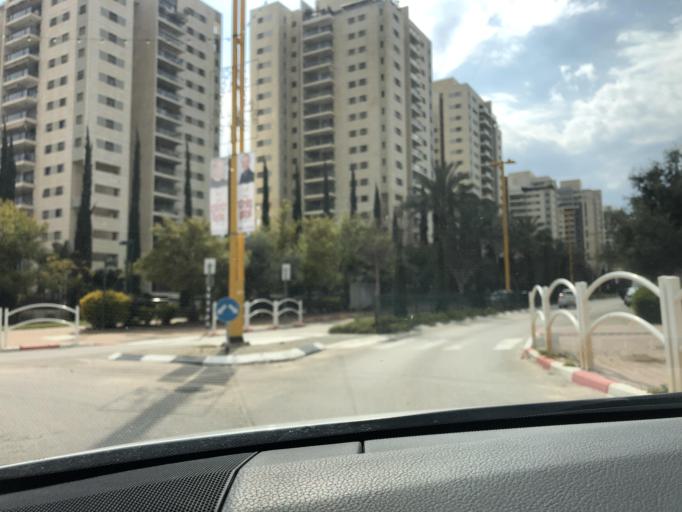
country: IL
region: Central District
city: Ganne Tiqwa
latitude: 32.0647
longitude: 34.8723
